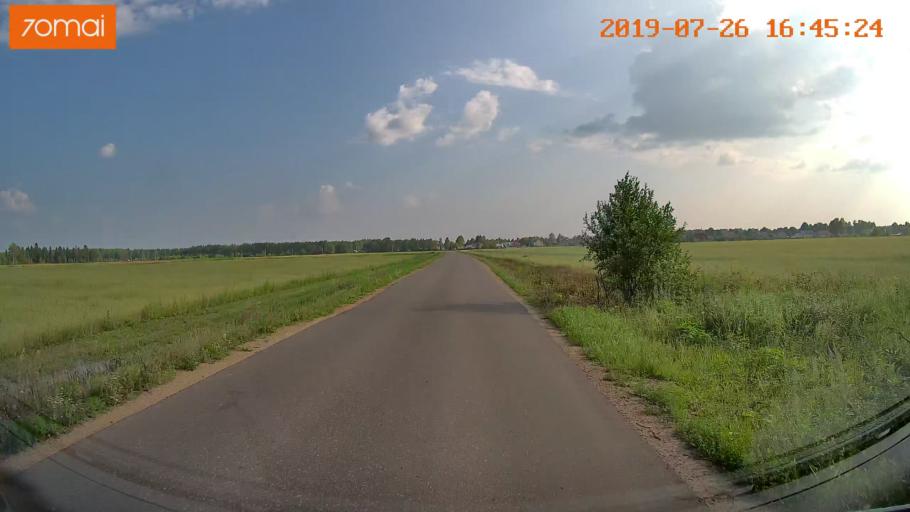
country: RU
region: Ivanovo
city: Bogorodskoye
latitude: 57.0505
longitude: 41.0220
